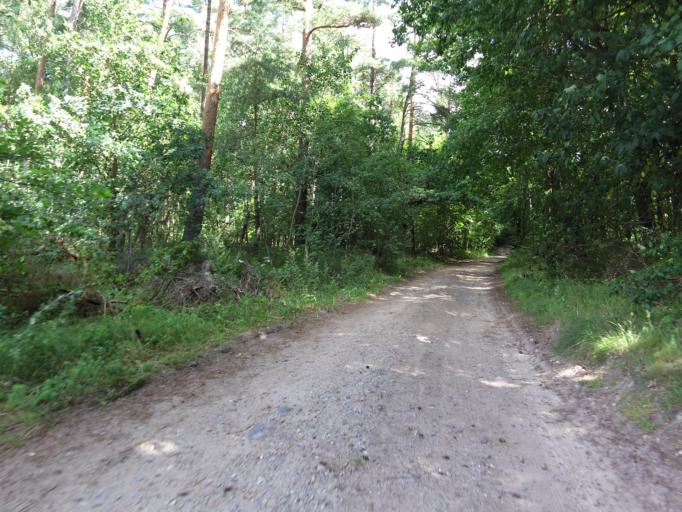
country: DE
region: Brandenburg
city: Lychen
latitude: 53.2220
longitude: 13.3309
